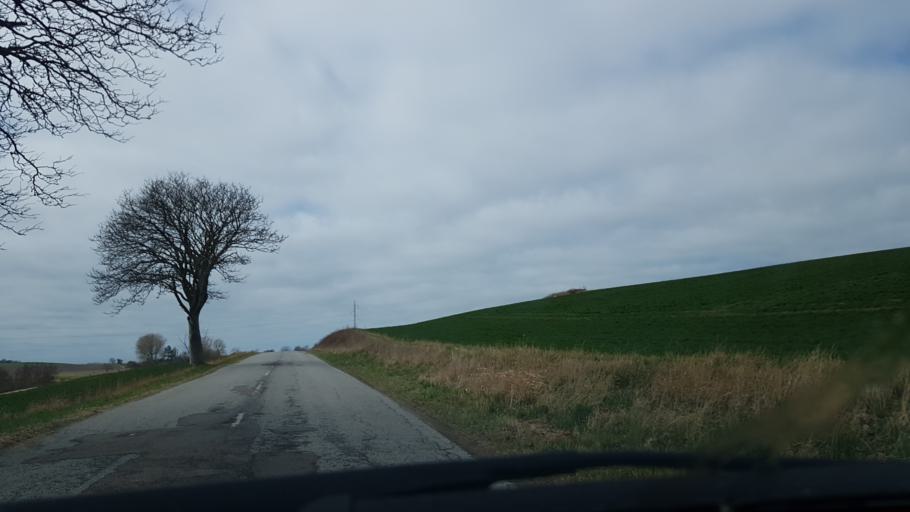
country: DK
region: Zealand
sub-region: Odsherred Kommune
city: Hojby
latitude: 55.9182
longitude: 11.5780
